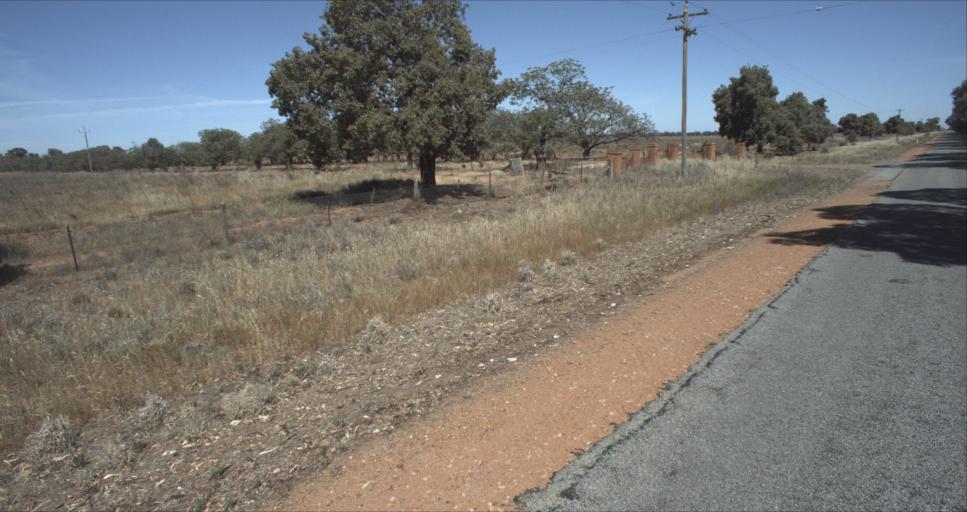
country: AU
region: New South Wales
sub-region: Leeton
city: Leeton
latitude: -34.5789
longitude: 146.2722
